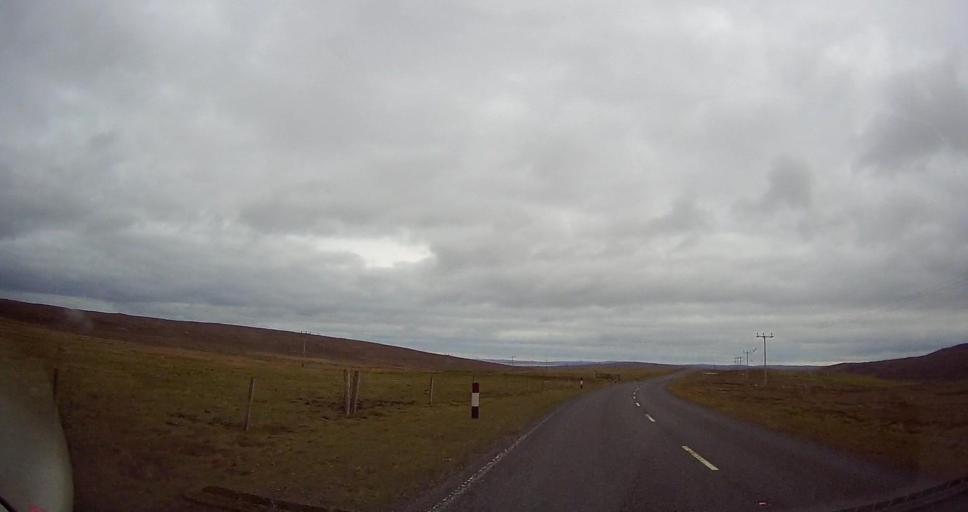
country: GB
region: Scotland
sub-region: Shetland Islands
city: Shetland
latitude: 60.7318
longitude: -0.8956
